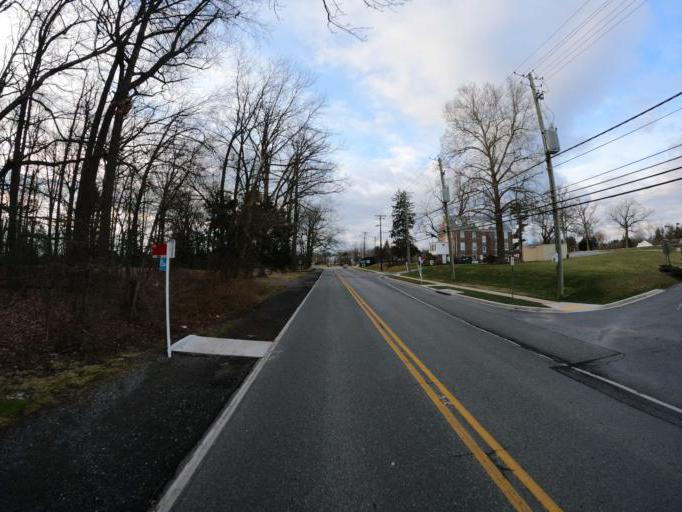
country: US
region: Maryland
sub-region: Montgomery County
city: Olney
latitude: 39.1510
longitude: -77.0573
